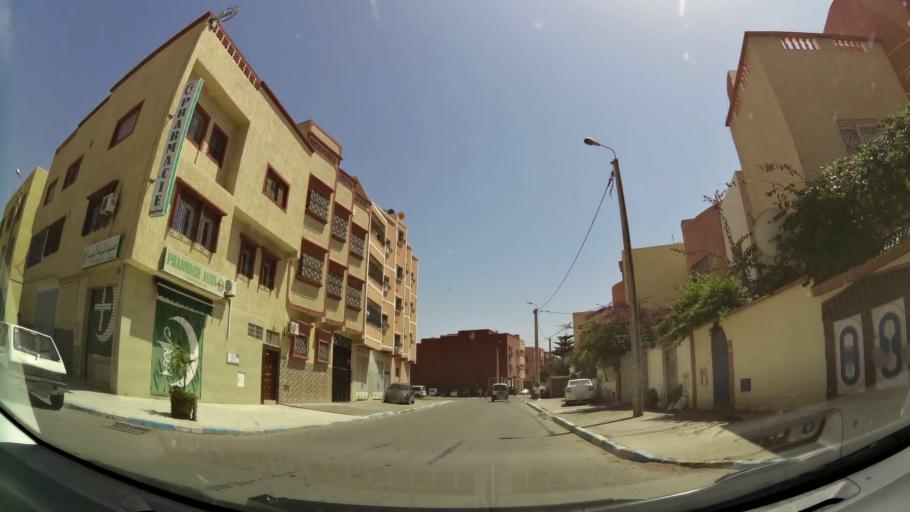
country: MA
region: Souss-Massa-Draa
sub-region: Inezgane-Ait Mellou
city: Inezgane
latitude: 30.3524
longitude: -9.4897
